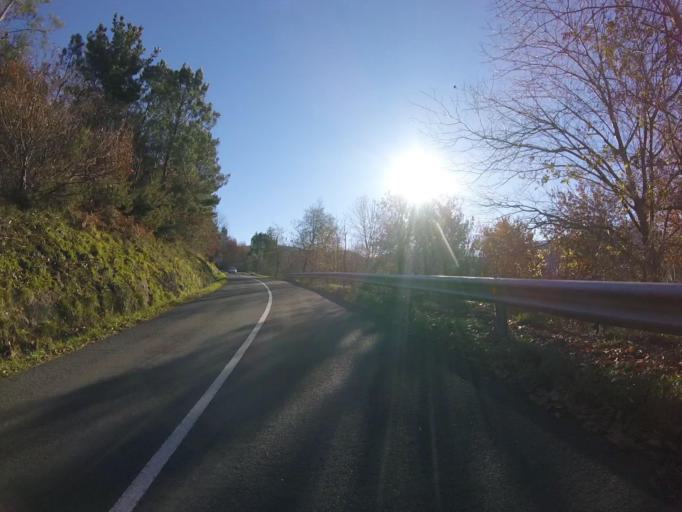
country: ES
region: Basque Country
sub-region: Provincia de Guipuzcoa
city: Irun
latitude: 43.3197
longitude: -1.7705
